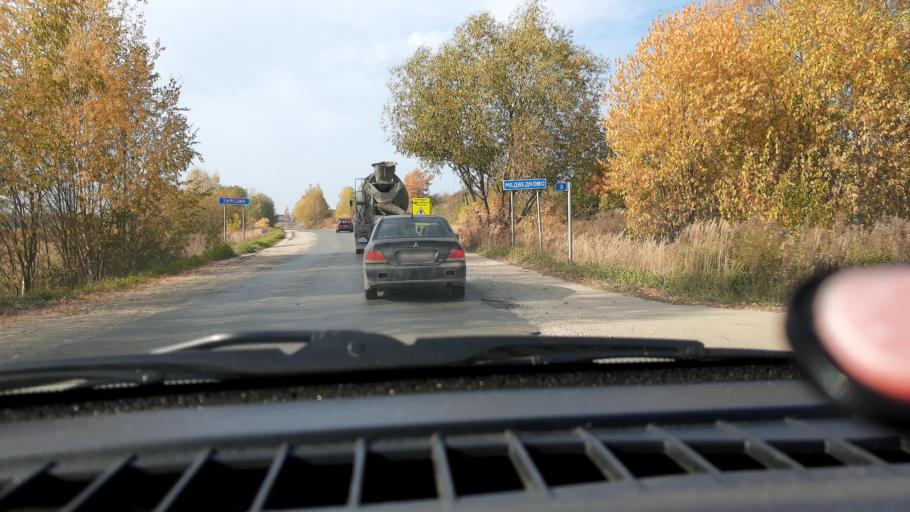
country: RU
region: Nizjnij Novgorod
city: Neklyudovo
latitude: 56.4203
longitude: 43.9621
